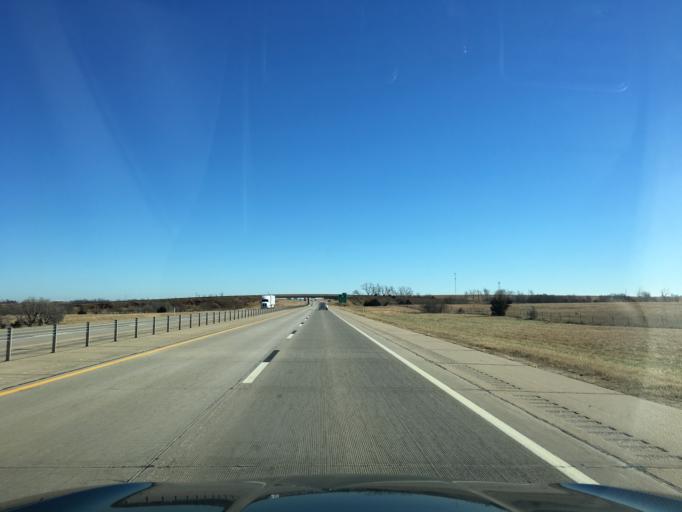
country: US
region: Oklahoma
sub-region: Noble County
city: Perry
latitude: 36.3877
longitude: -97.0899
